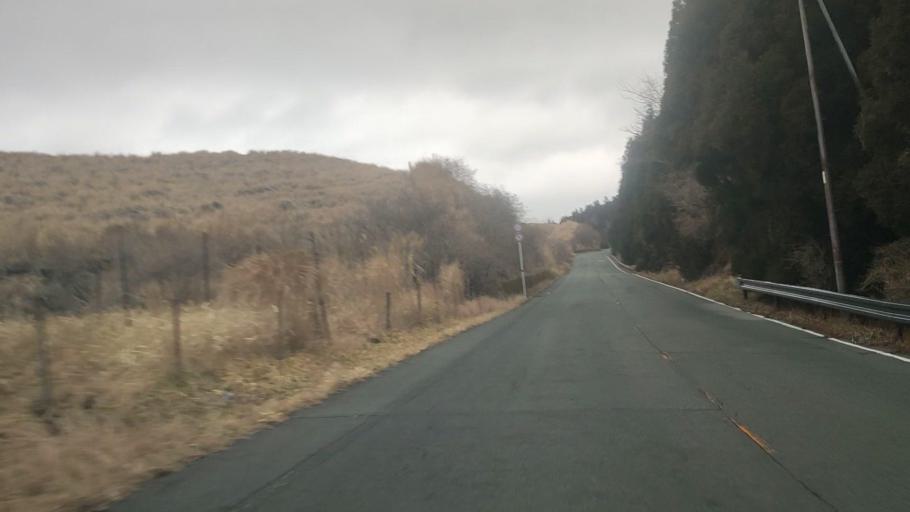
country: JP
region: Kumamoto
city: Aso
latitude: 32.8810
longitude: 131.1704
